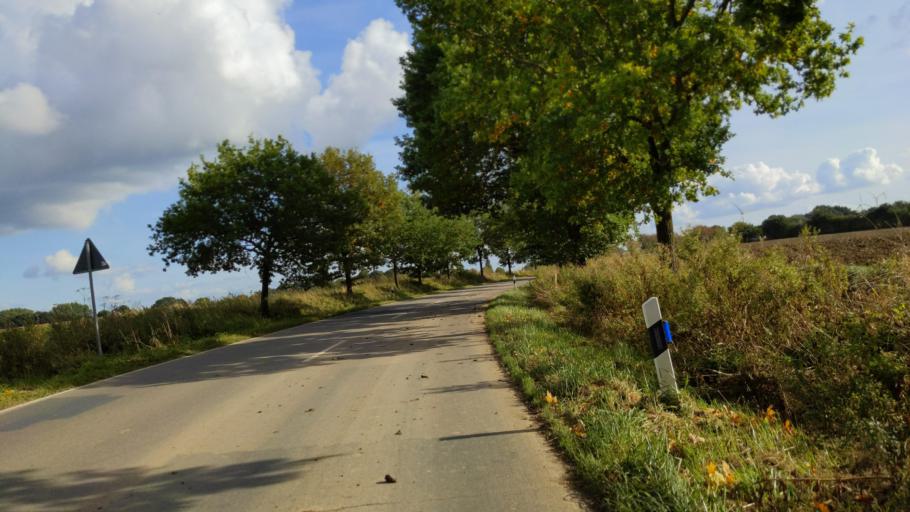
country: DE
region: Schleswig-Holstein
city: Ahrensbok
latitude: 54.0206
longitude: 10.6408
